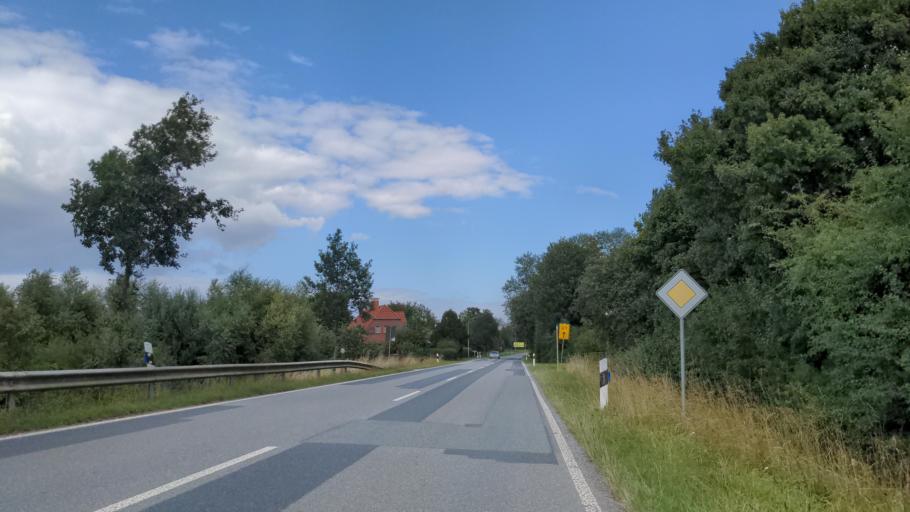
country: DE
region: Schleswig-Holstein
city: Beschendorf
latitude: 54.1766
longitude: 10.8759
